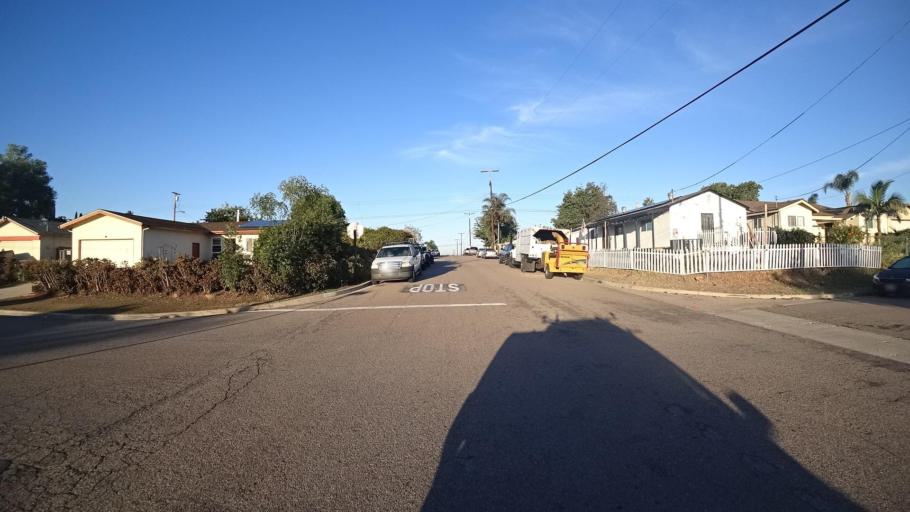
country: US
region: California
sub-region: San Diego County
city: La Presa
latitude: 32.7097
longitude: -116.9949
